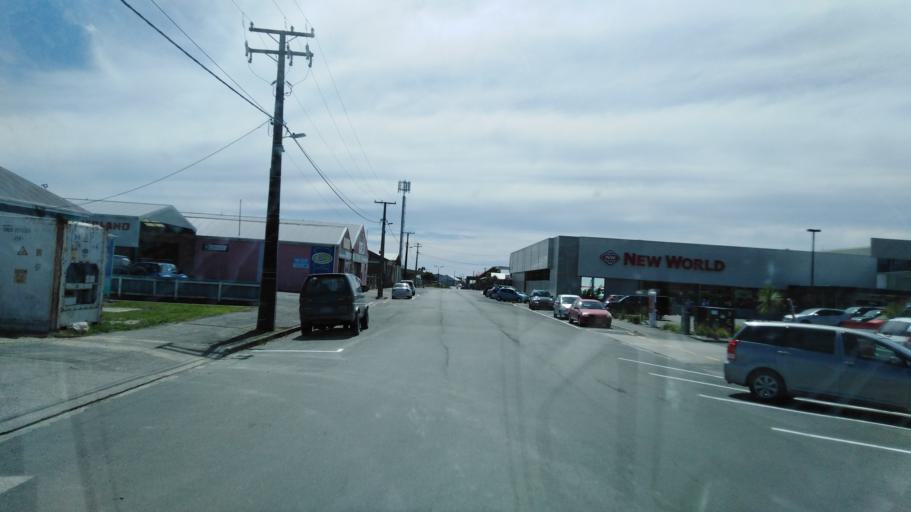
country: NZ
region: West Coast
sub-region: Buller District
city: Westport
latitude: -41.7582
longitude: 171.5986
